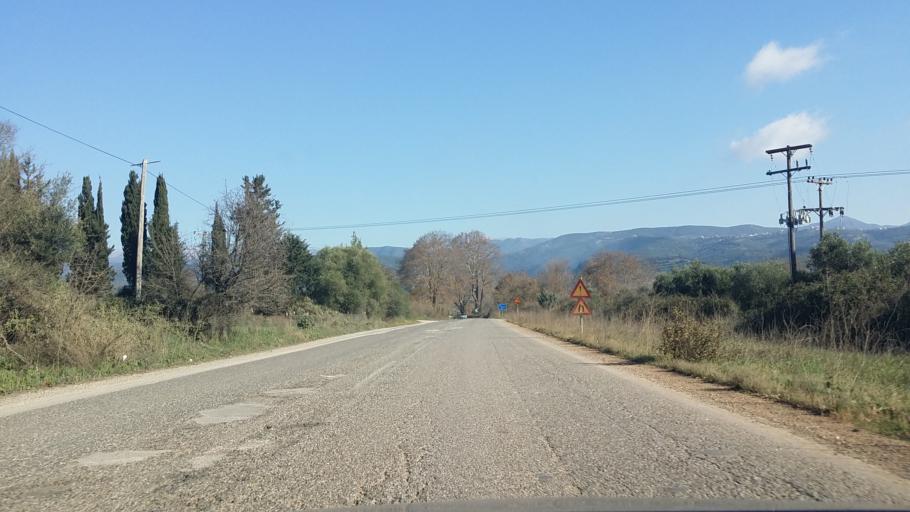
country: GR
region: West Greece
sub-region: Nomos Aitolias kai Akarnanias
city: Krikellos
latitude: 38.9174
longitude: 21.1763
